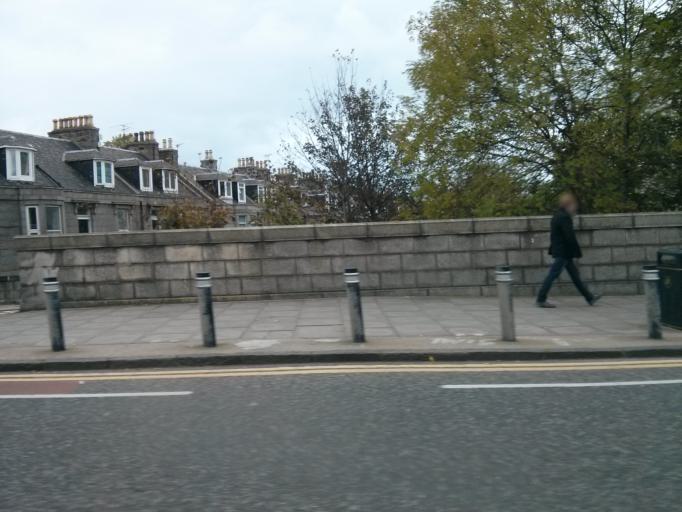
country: GB
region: Scotland
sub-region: Aberdeen City
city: Aberdeen
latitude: 57.1538
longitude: -2.0945
